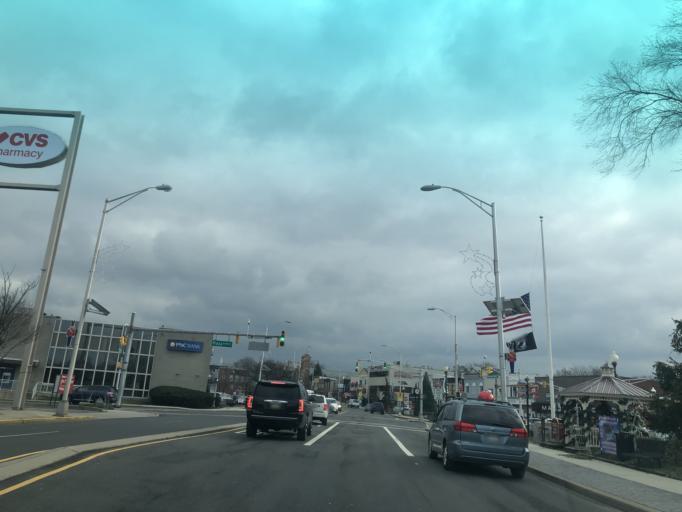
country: US
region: New Jersey
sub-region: Hudson County
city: Secaucus
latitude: 40.7908
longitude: -74.0579
